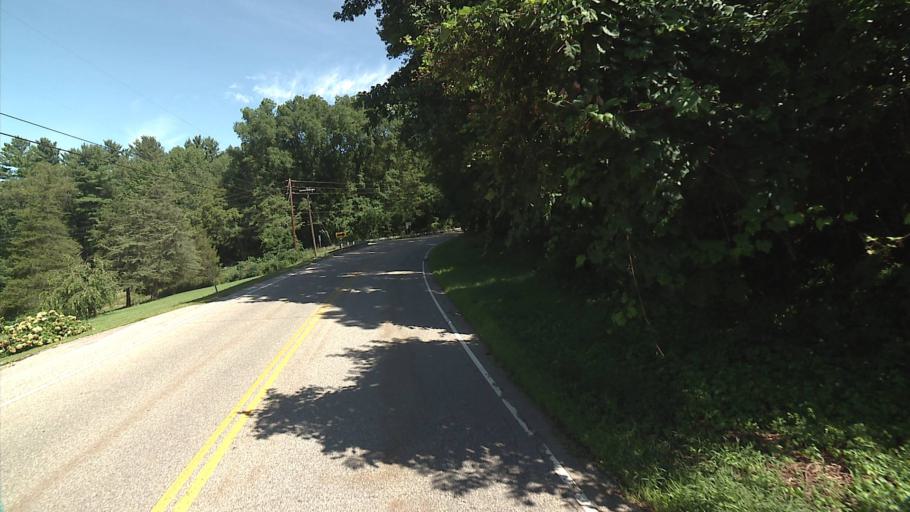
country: US
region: Connecticut
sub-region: New London County
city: Baltic
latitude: 41.6565
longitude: -72.0926
